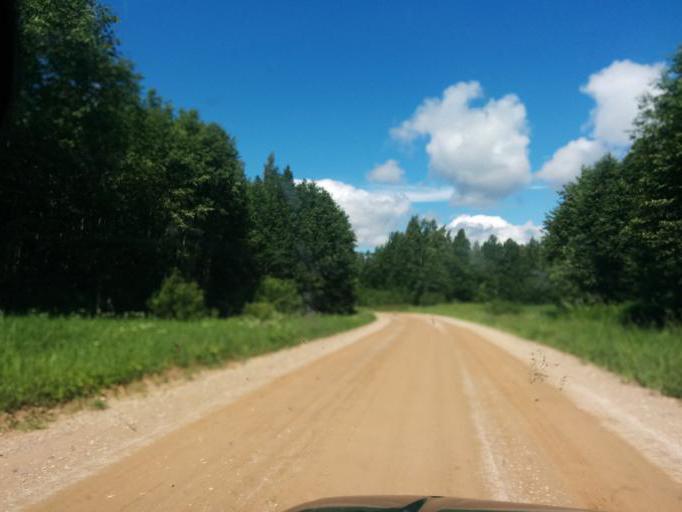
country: LV
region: Vilaka
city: Vilaka
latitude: 57.3733
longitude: 27.4685
